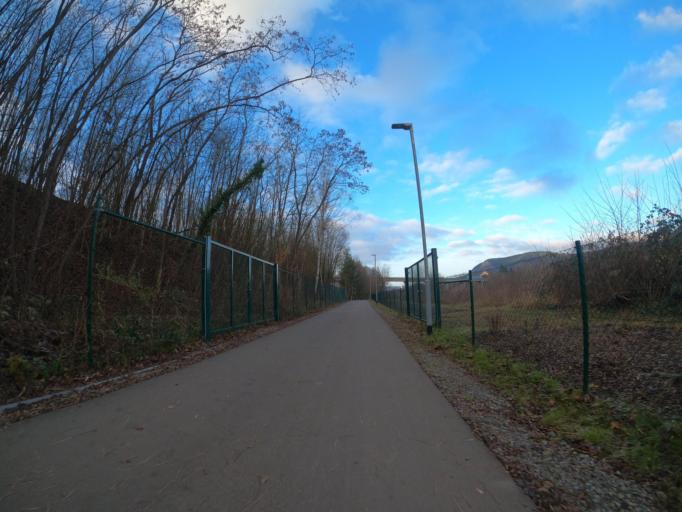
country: DE
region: Thuringia
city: Sulza
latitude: 50.8921
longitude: 11.5904
